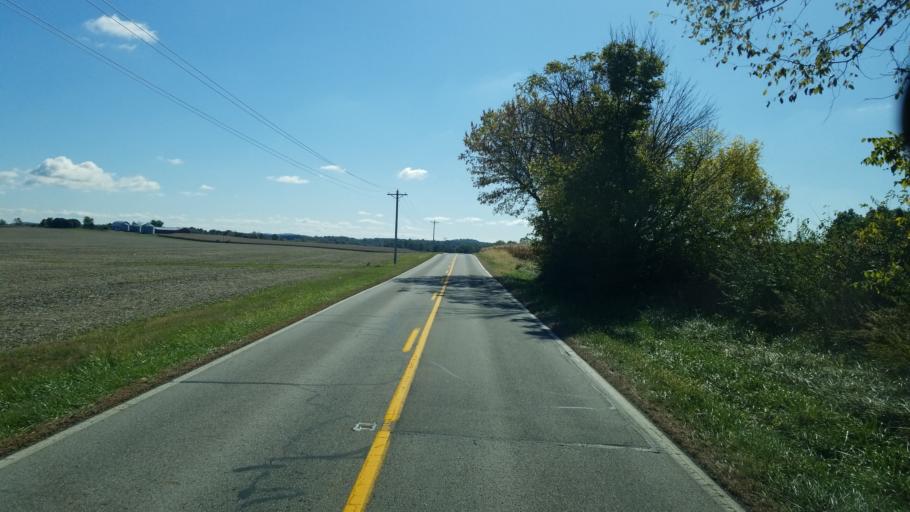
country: US
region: Ohio
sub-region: Highland County
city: Leesburg
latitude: 39.2847
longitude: -83.5002
